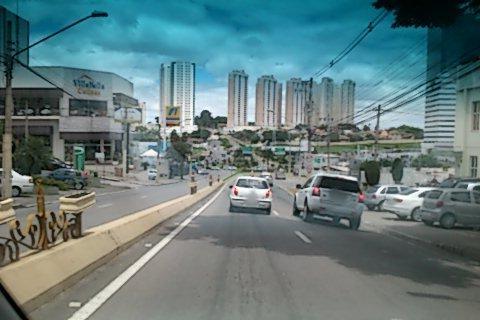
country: BR
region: Sao Paulo
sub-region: Sao Jose Dos Campos
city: Sao Jose dos Campos
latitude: -23.2039
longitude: -45.9047
